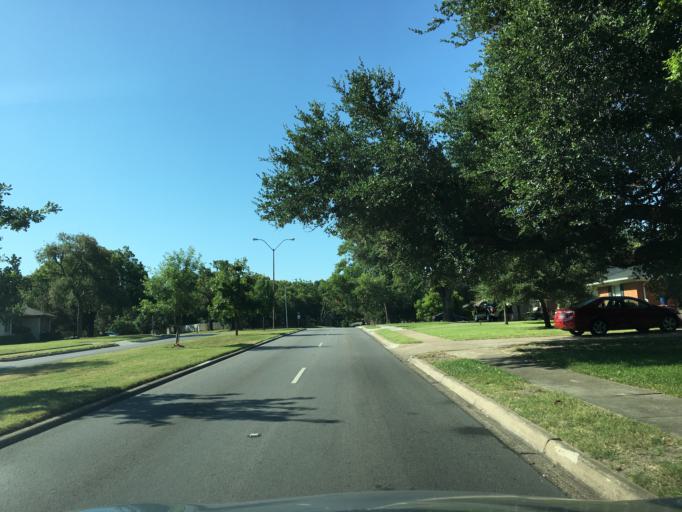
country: US
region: Texas
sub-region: Dallas County
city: Highland Park
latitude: 32.8615
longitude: -96.7102
